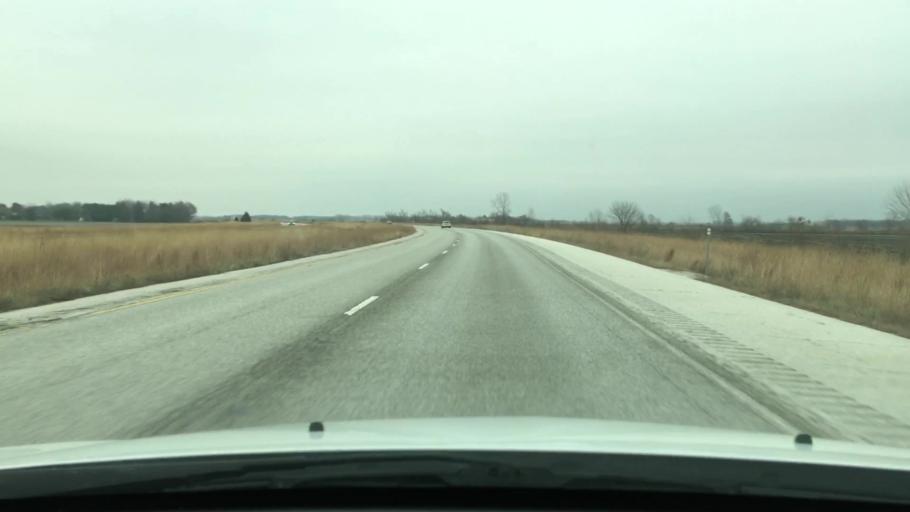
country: US
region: Illinois
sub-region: Morgan County
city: South Jacksonville
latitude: 39.6864
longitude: -90.2126
